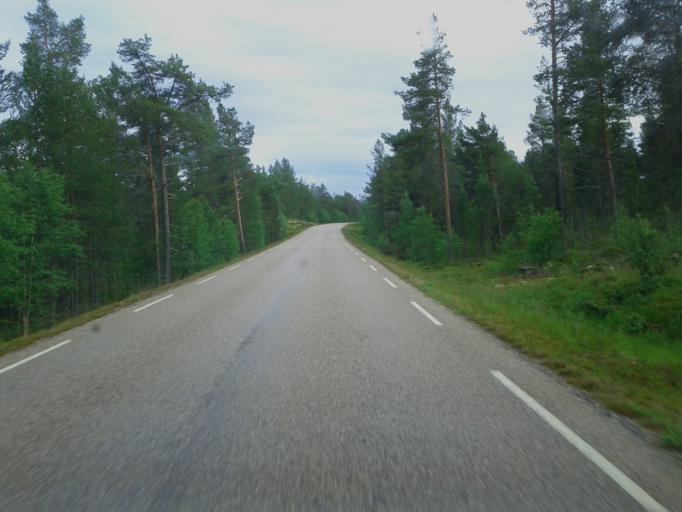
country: NO
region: Hedmark
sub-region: Engerdal
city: Engerdal
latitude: 62.0735
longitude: 11.6749
